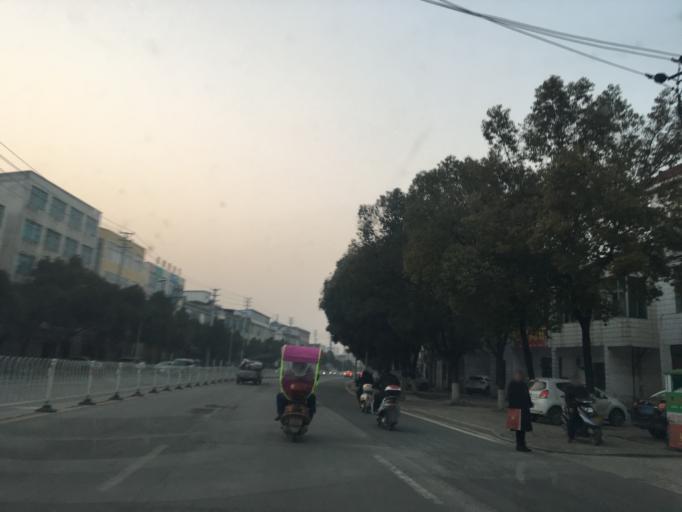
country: CN
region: Hubei
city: Gulou
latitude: 31.1704
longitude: 115.0284
